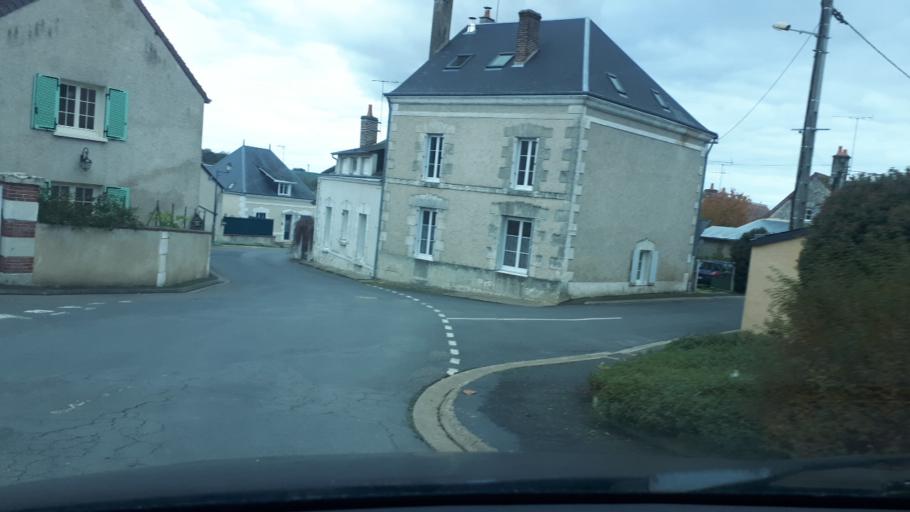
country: FR
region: Centre
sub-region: Departement du Loir-et-Cher
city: Villiers-sur-Loir
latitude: 47.7885
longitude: 0.9648
